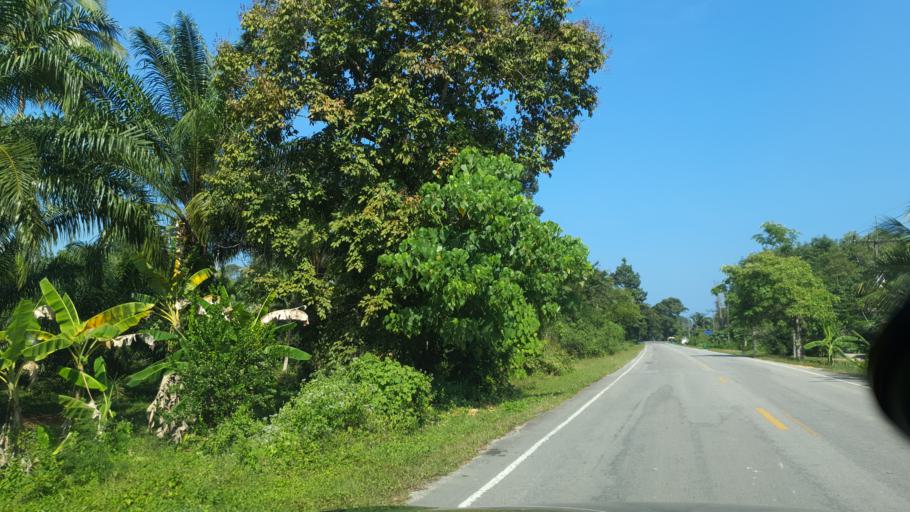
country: TH
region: Surat Thani
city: Tha Chana
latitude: 9.5750
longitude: 99.1824
